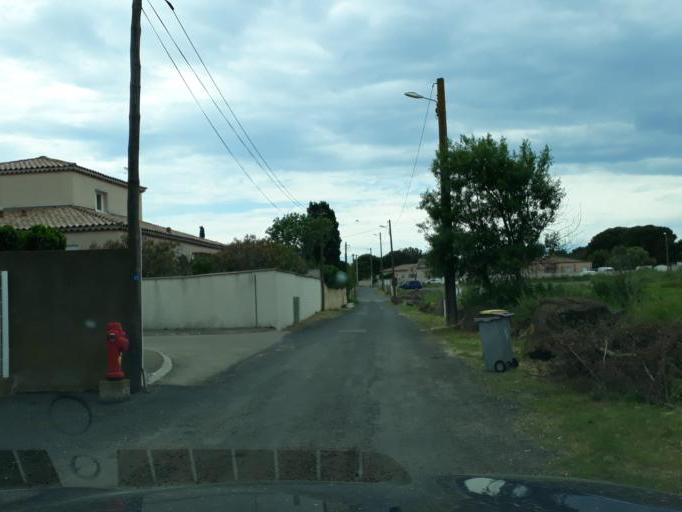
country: FR
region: Languedoc-Roussillon
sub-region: Departement de l'Herault
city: Agde
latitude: 43.2924
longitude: 3.4638
